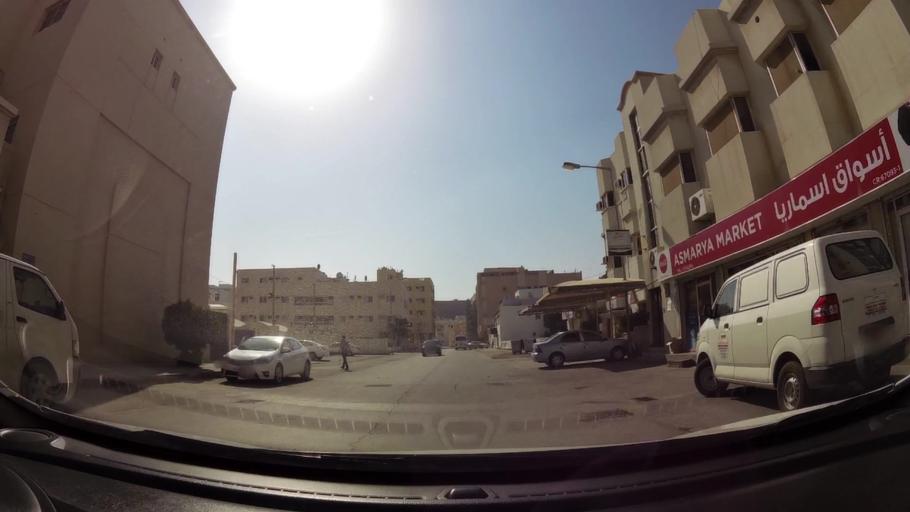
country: BH
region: Manama
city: Manama
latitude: 26.2092
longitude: 50.5908
